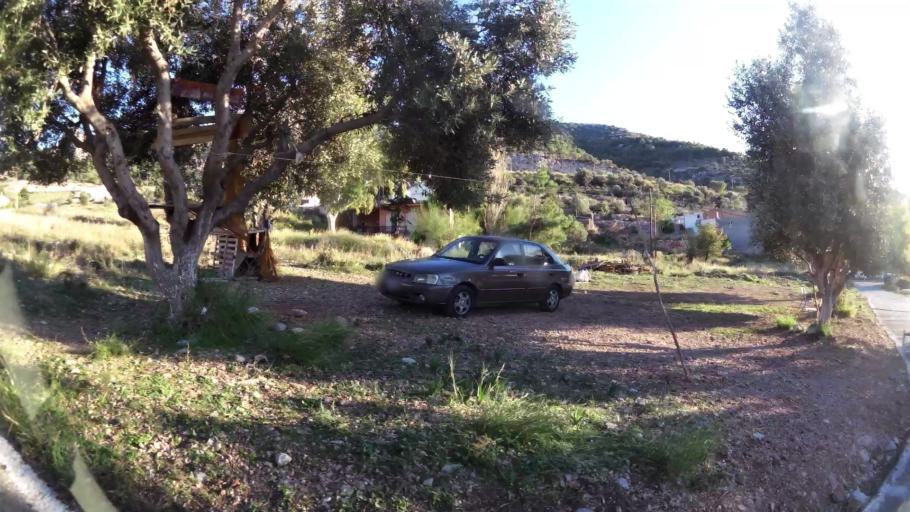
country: GR
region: Attica
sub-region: Nomarchia Athinas
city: Skaramangas
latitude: 38.0284
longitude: 23.6190
